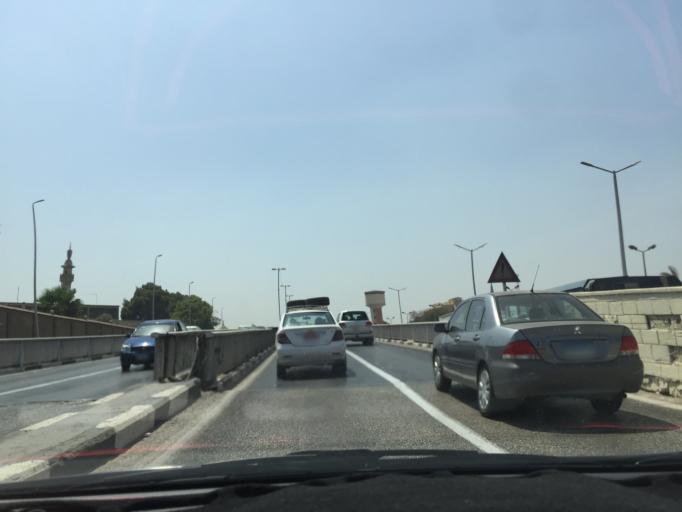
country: EG
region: Muhafazat al Qahirah
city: Cairo
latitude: 30.0573
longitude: 31.2812
